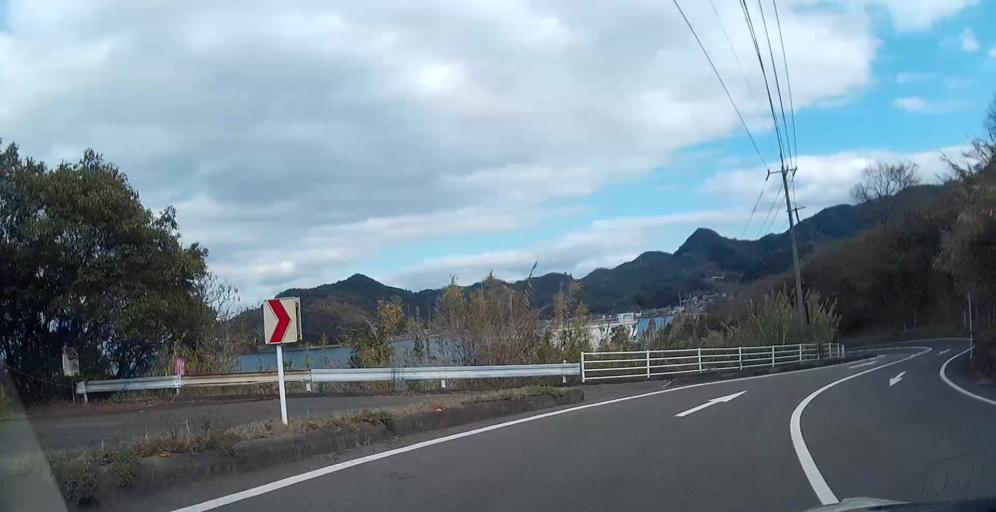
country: JP
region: Kumamoto
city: Minamata
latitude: 32.3270
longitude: 130.4767
